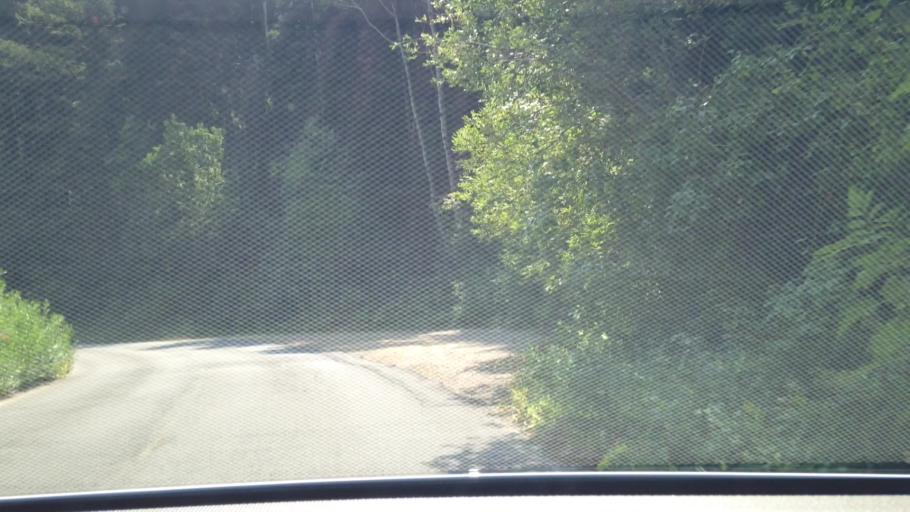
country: US
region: Utah
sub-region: Summit County
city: Summit Park
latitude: 40.6893
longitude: -111.6640
